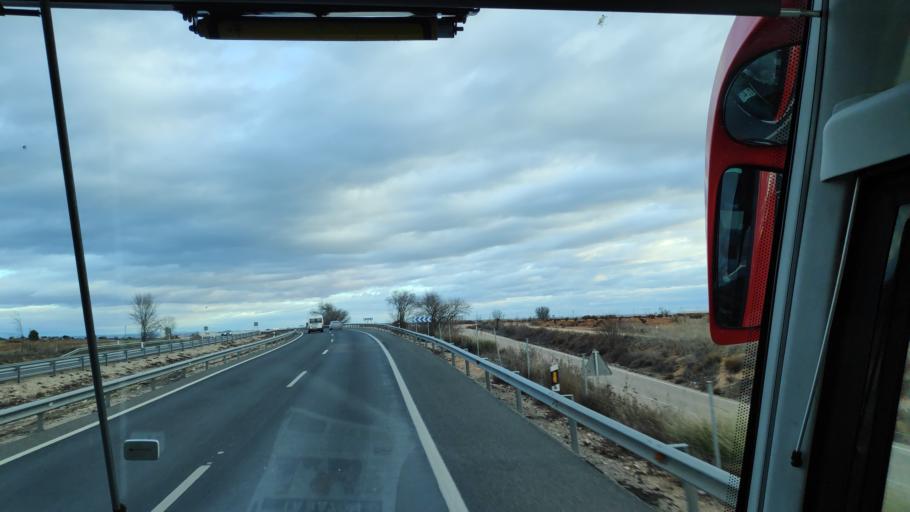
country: ES
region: Madrid
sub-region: Provincia de Madrid
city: Villarejo de Salvanes
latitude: 40.1584
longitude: -3.2606
